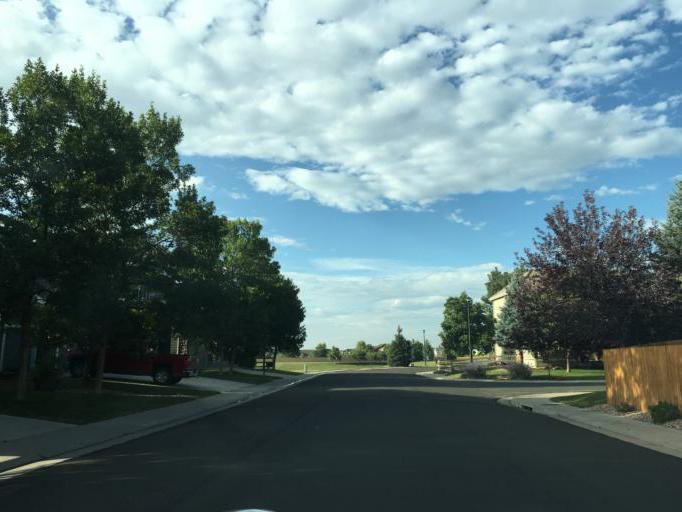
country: US
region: Colorado
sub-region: Adams County
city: Northglenn
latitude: 39.9480
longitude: -104.9550
